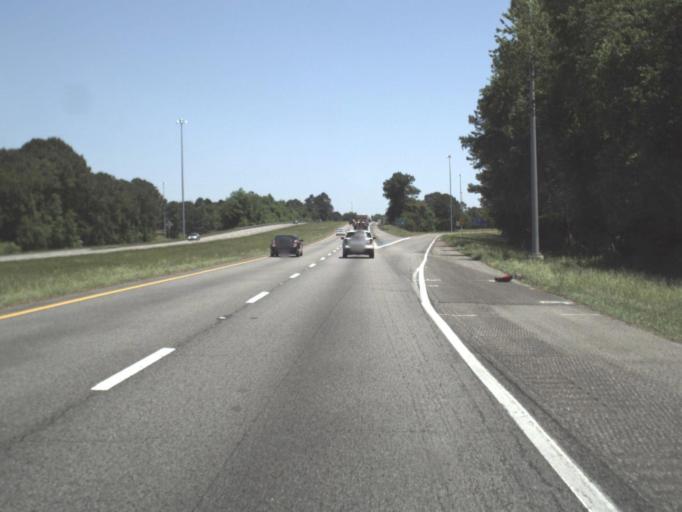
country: US
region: Florida
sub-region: Jefferson County
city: Monticello
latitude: 30.4570
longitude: -83.7684
